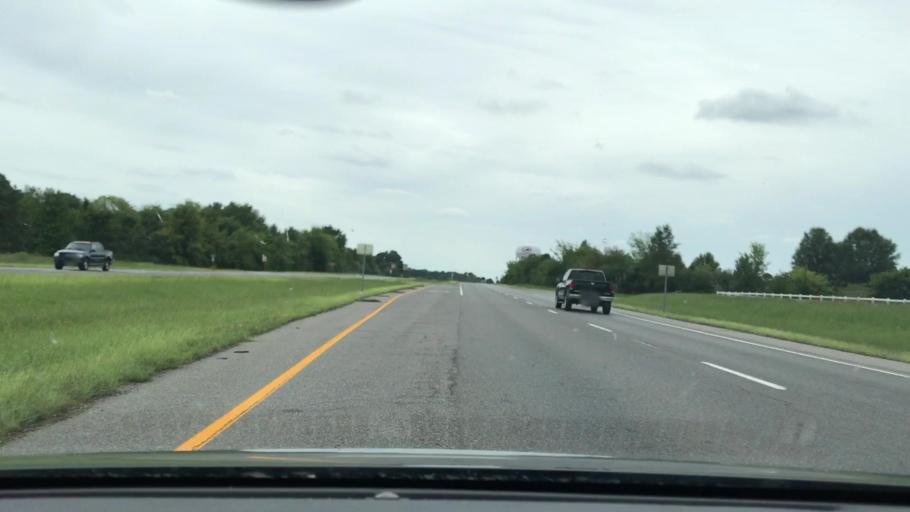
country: US
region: Kentucky
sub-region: Marshall County
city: Benton
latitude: 36.8331
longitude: -88.3753
